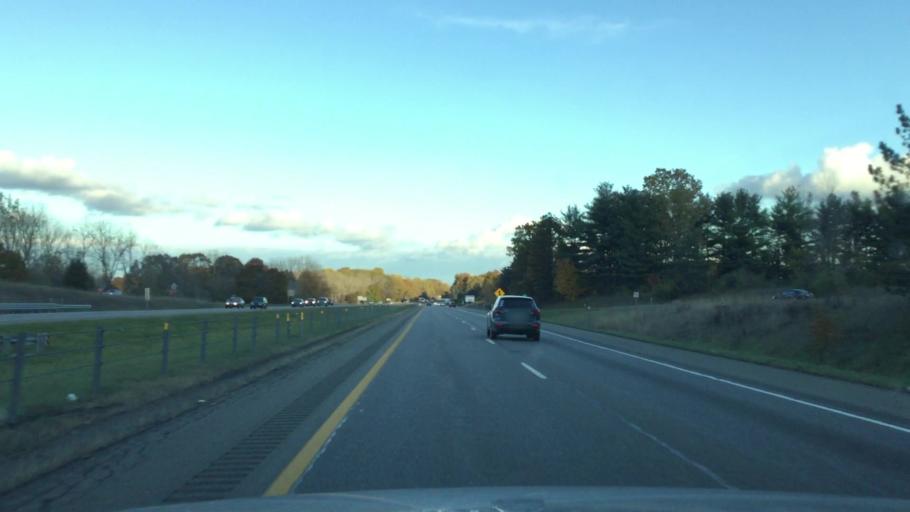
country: US
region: Michigan
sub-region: Calhoun County
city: Lakeview
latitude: 42.2651
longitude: -85.2377
